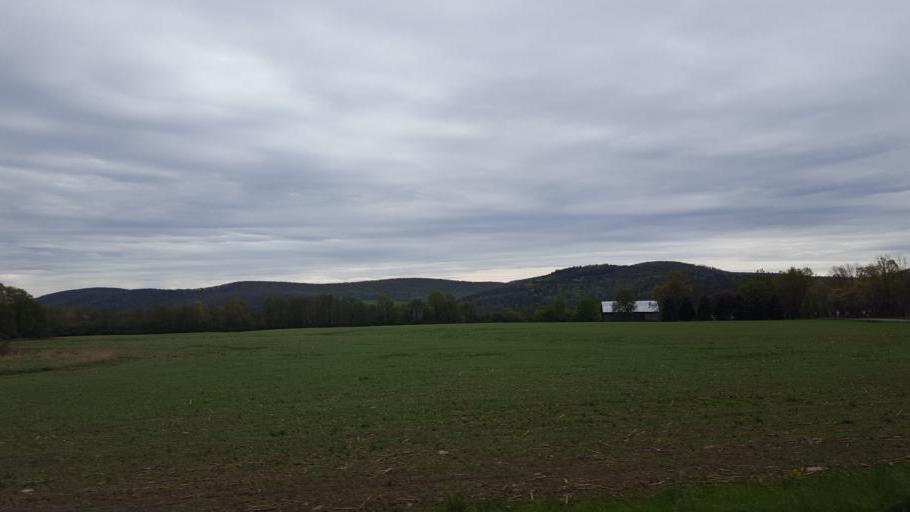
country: US
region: Pennsylvania
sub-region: Tioga County
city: Westfield
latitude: 42.0021
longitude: -77.4868
